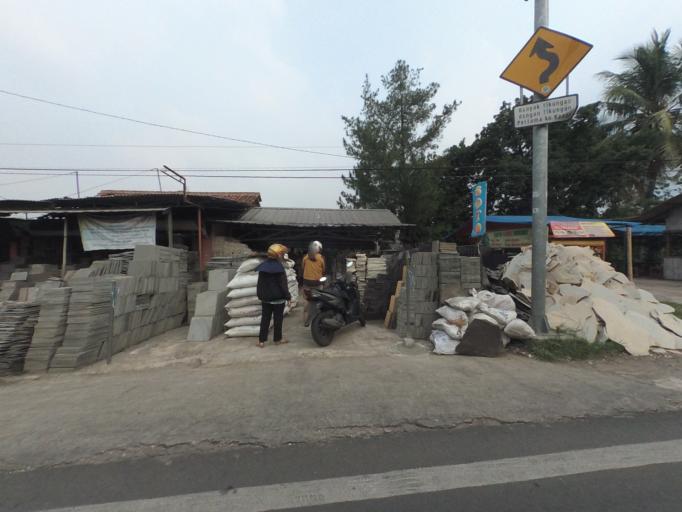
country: ID
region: West Java
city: Ciampea
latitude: -6.5614
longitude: 106.6851
